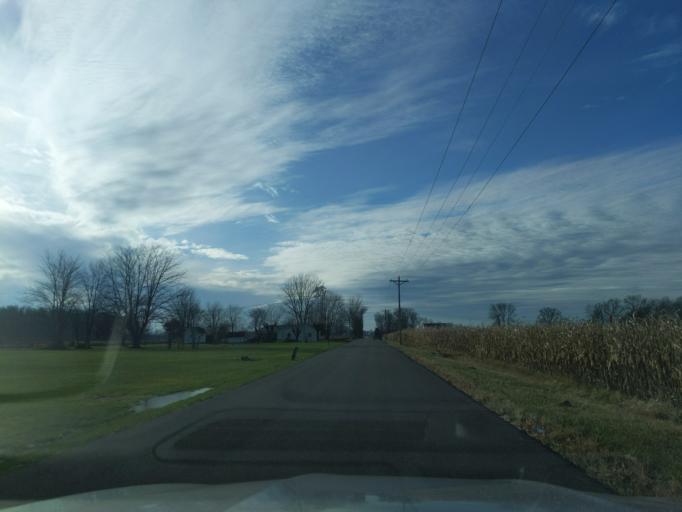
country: US
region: Indiana
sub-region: Decatur County
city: Westport
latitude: 39.1834
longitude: -85.5512
